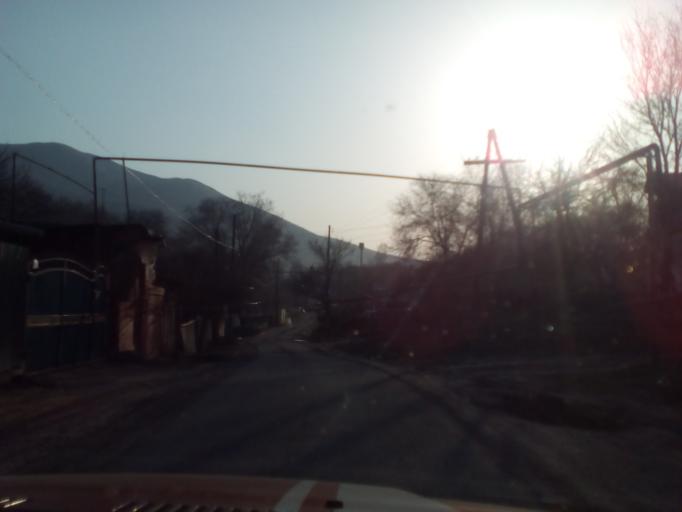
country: KZ
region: Almaty Oblysy
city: Burunday
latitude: 43.1576
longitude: 76.4365
